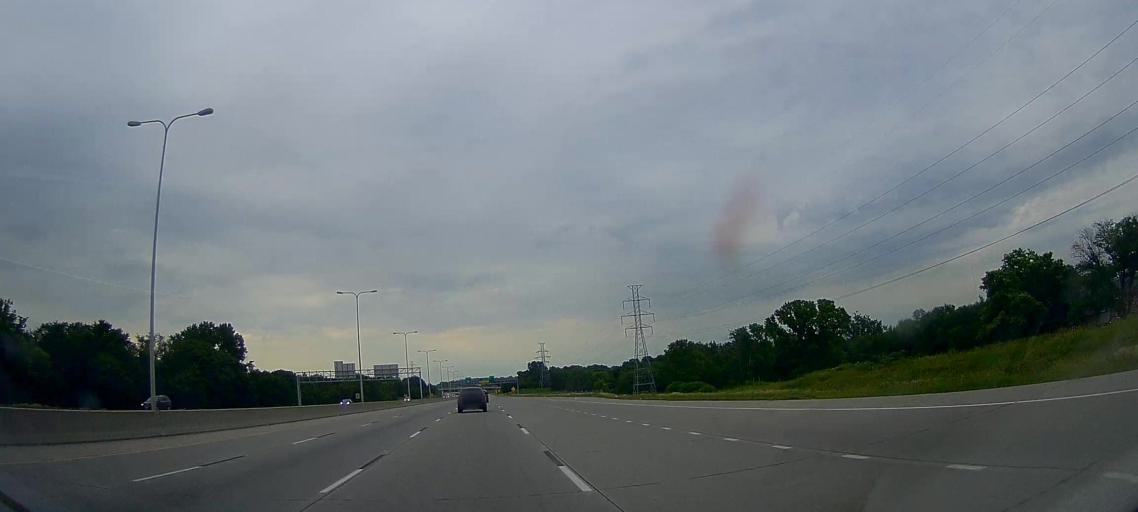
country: US
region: Nebraska
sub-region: Douglas County
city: Ralston
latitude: 41.2901
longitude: -96.0740
